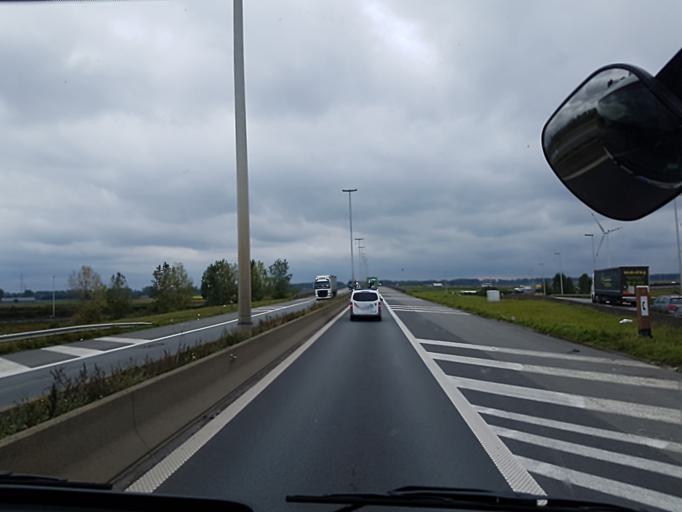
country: BE
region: Flanders
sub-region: Provincie Oost-Vlaanderen
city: Beveren
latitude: 51.2442
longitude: 4.2496
